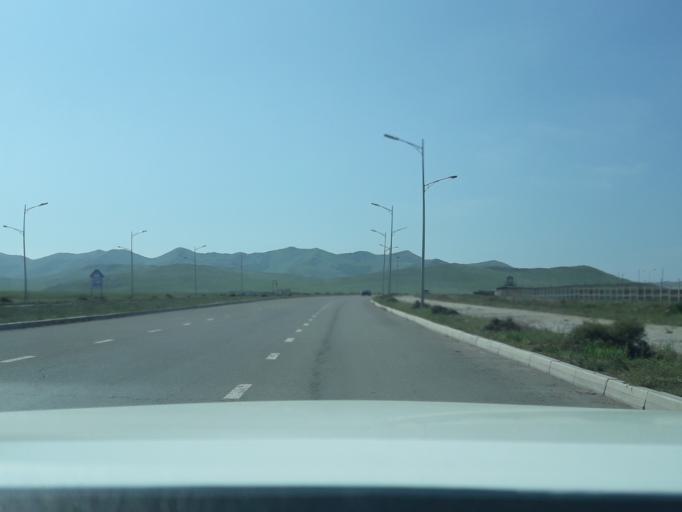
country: MN
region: Ulaanbaatar
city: Ulaanbaatar
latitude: 47.8321
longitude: 106.7868
